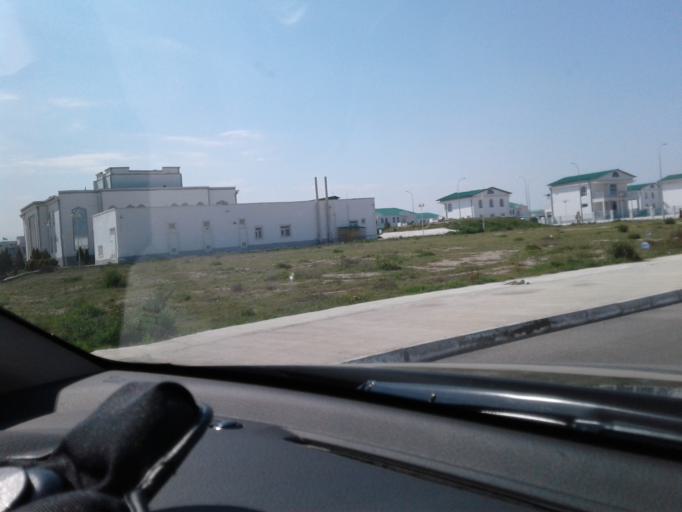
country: TM
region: Ahal
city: Abadan
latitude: 38.0784
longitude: 58.2826
